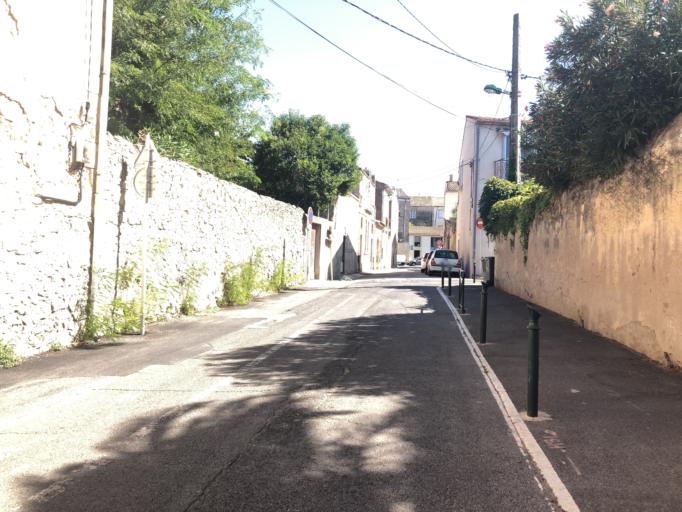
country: FR
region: Languedoc-Roussillon
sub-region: Departement de l'Herault
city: Meze
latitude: 43.4290
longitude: 3.6061
